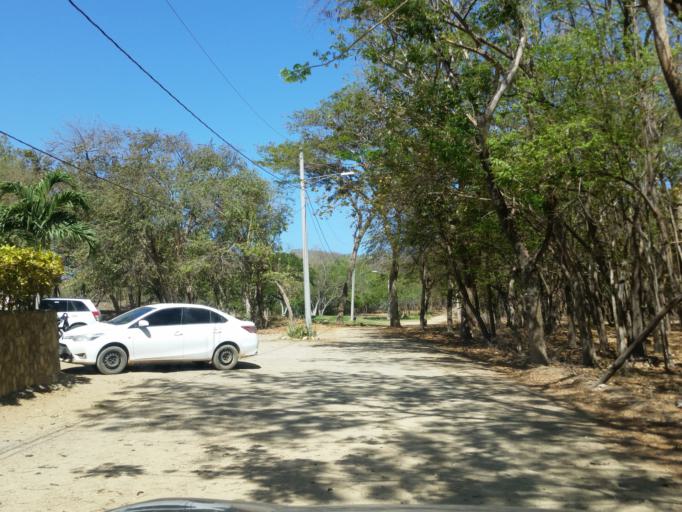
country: NI
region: Rivas
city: Tola
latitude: 11.4142
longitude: -86.0518
